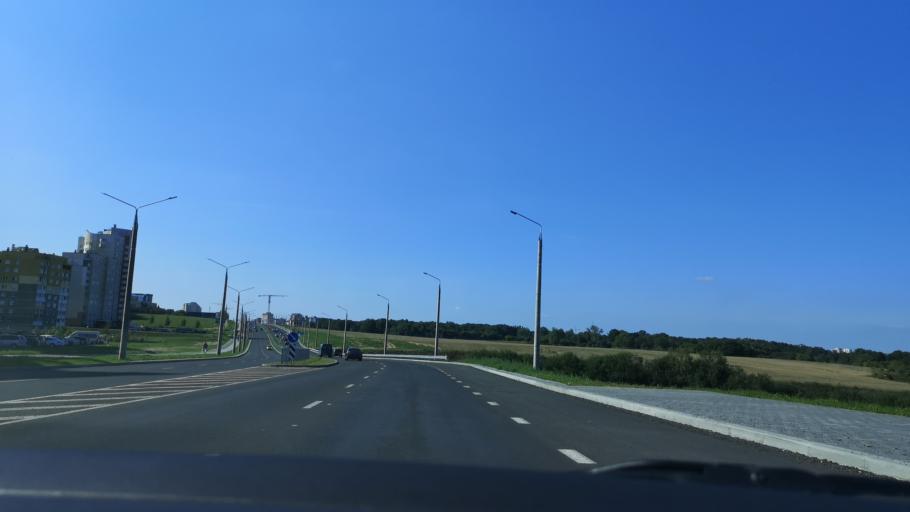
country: BY
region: Grodnenskaya
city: Hrodna
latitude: 53.6450
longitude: 23.8718
